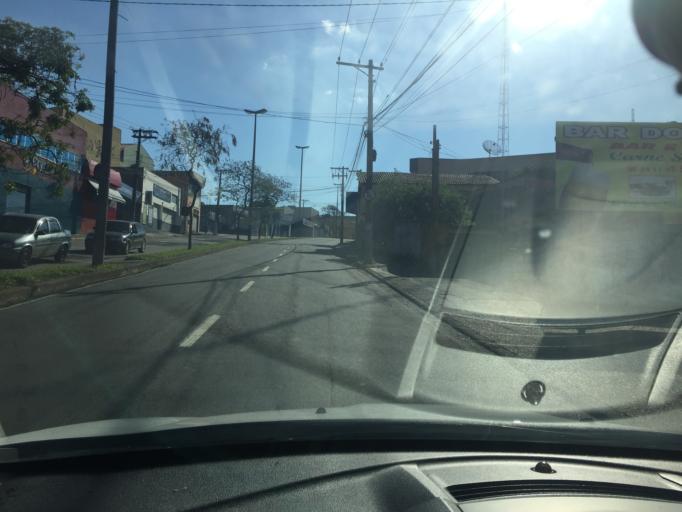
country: BR
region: Sao Paulo
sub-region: Varzea Paulista
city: Varzea Paulista
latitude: -23.2077
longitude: -46.8561
